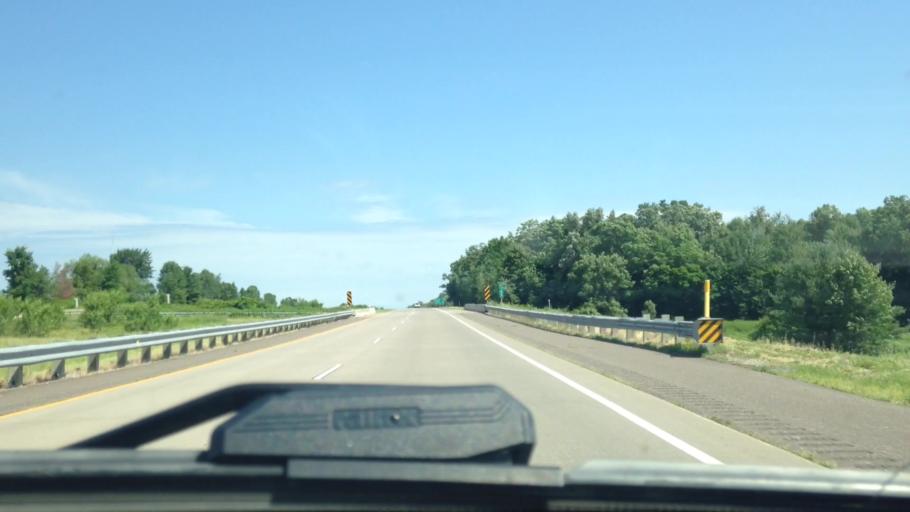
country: US
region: Wisconsin
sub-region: Barron County
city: Rice Lake
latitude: 45.5298
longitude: -91.7596
